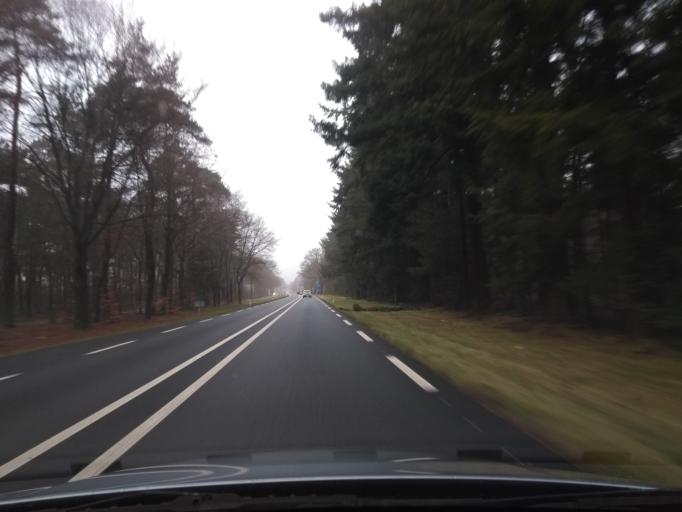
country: NL
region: Gelderland
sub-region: Gemeente Lochem
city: Almen
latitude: 52.1415
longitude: 6.3298
